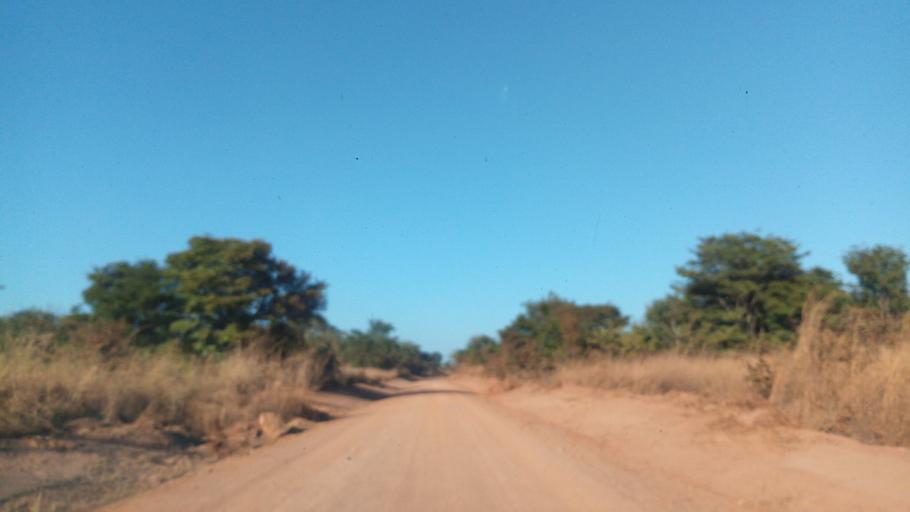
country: ZM
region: Luapula
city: Mwense
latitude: -10.4735
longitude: 28.5146
